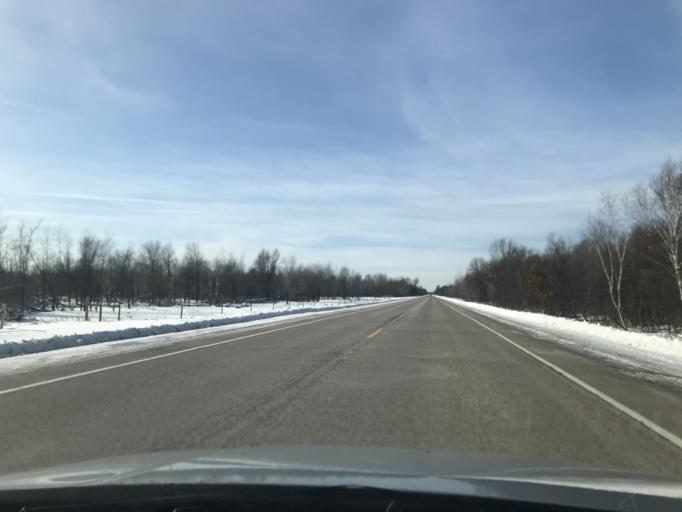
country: US
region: Wisconsin
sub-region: Oconto County
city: Gillett
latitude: 45.1140
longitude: -88.3229
